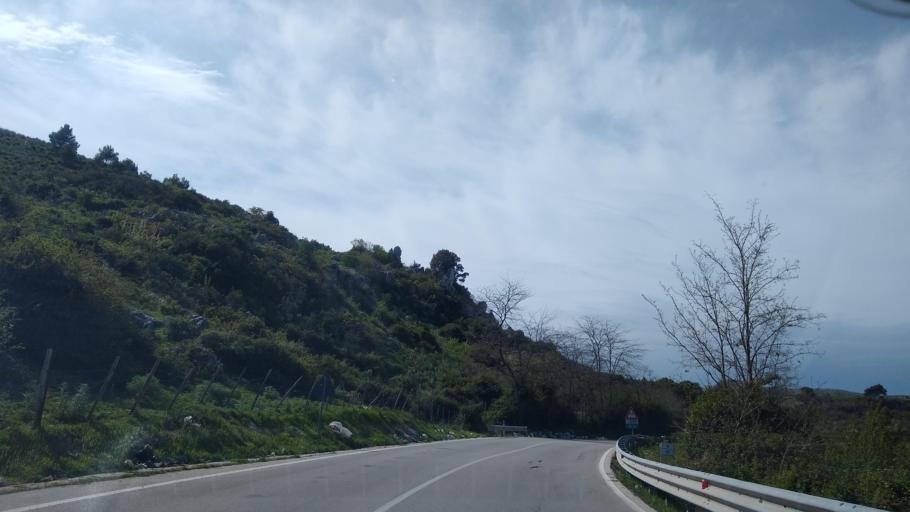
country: IT
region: Sicily
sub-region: Palermo
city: Pioppo
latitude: 38.0383
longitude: 13.2052
